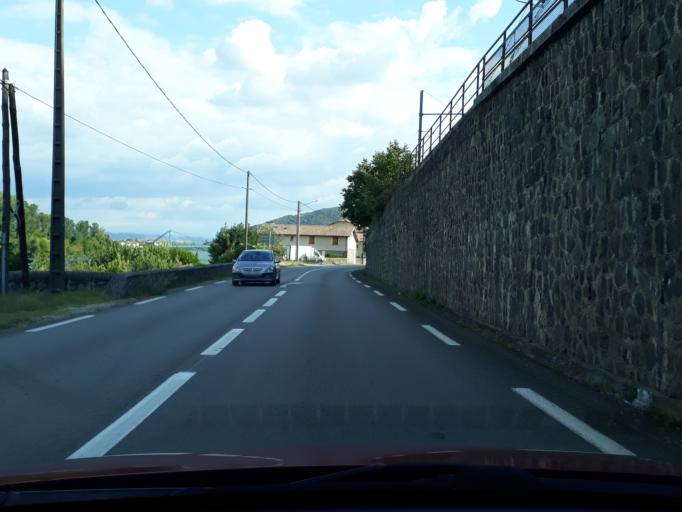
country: FR
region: Rhone-Alpes
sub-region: Departement de l'Ardeche
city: Serrieres
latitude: 45.3256
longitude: 4.7587
